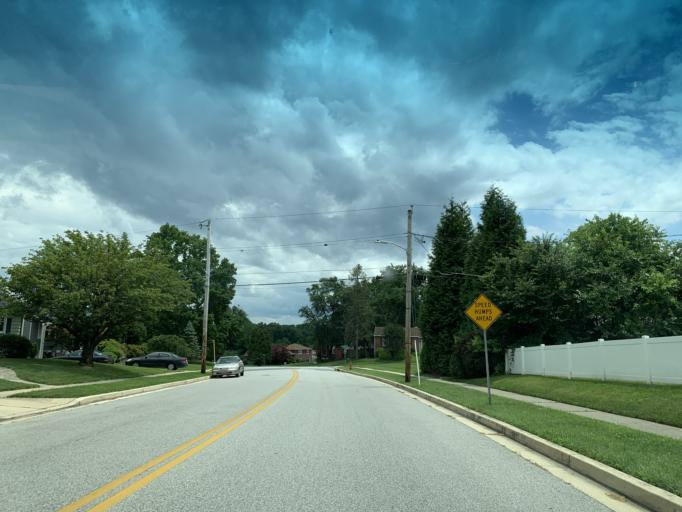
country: US
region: Maryland
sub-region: Baltimore County
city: Timonium
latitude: 39.4452
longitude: -76.6153
